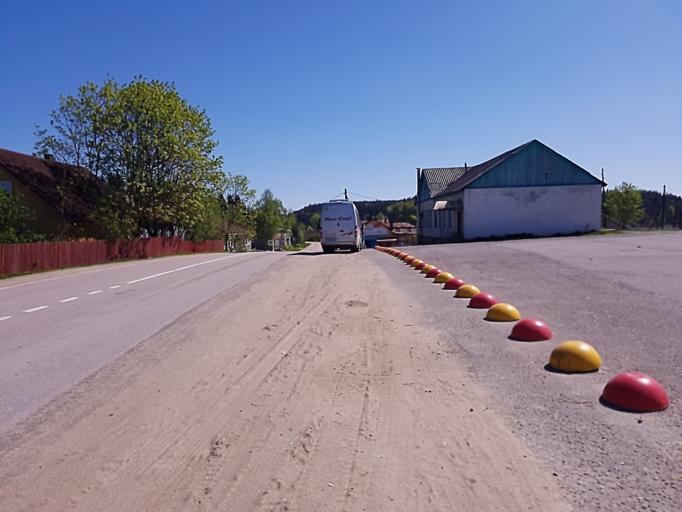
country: RU
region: Leningrad
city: Kuznechnoye
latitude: 61.2991
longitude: 29.8901
